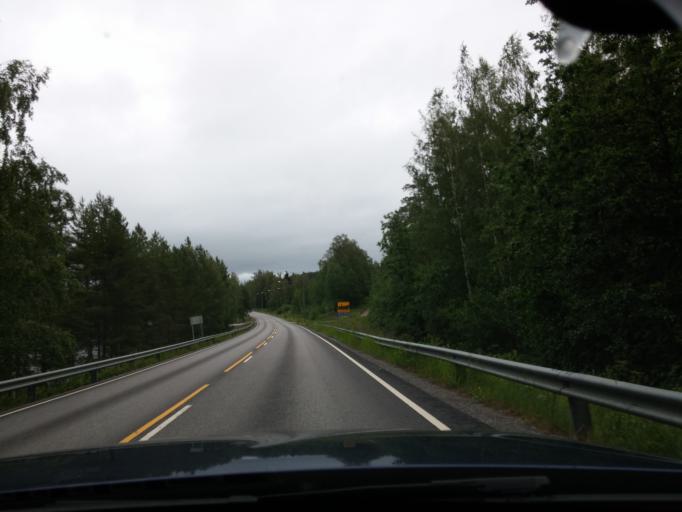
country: FI
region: Central Finland
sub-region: Saarijaervi-Viitasaari
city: Saarijaervi
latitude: 62.6911
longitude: 25.2745
